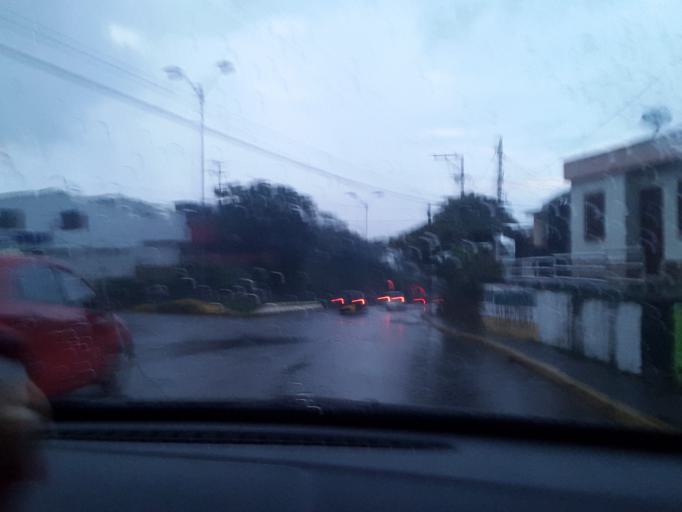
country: CO
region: Quindio
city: Armenia
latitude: 4.5309
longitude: -75.6952
